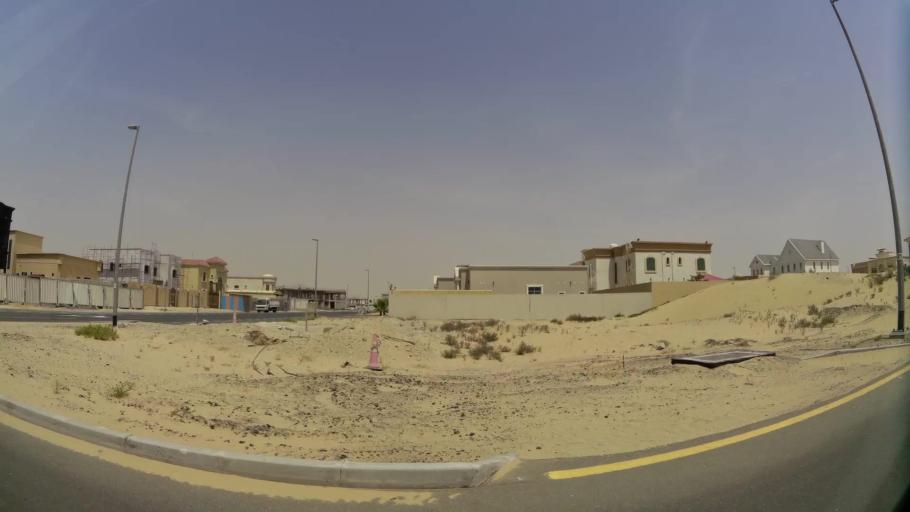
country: AE
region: Ash Shariqah
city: Sharjah
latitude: 25.2521
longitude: 55.5044
